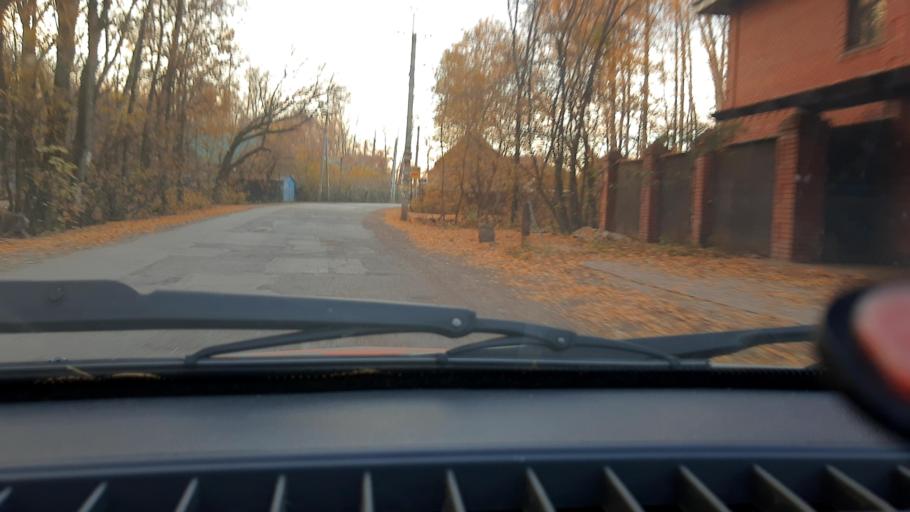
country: RU
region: Bashkortostan
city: Ufa
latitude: 54.6974
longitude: 55.9018
